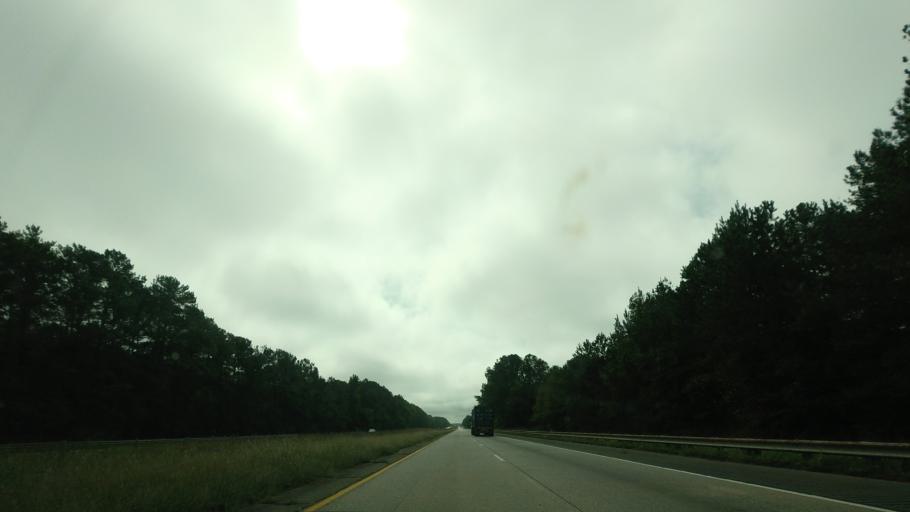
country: US
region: Georgia
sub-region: Bibb County
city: Macon
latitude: 32.7561
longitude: -83.5525
